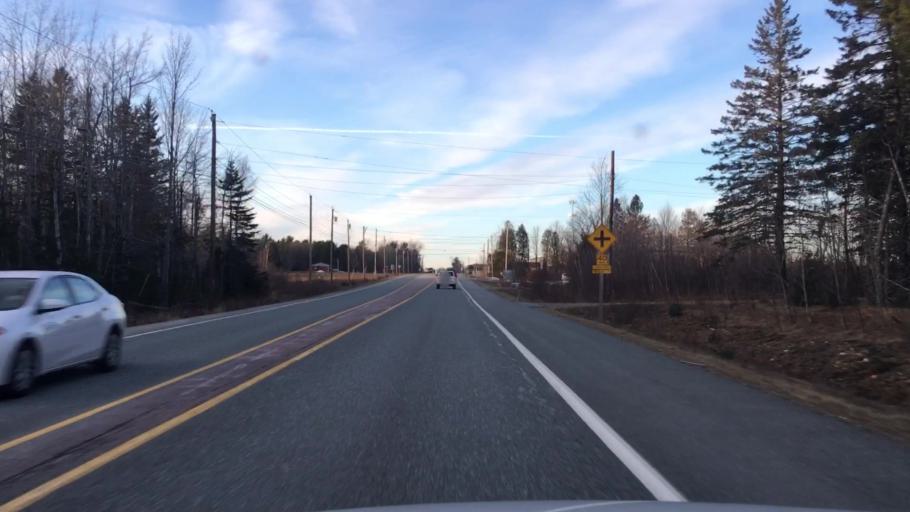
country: US
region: Maine
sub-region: Hancock County
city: Surry
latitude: 44.6134
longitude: -68.5229
